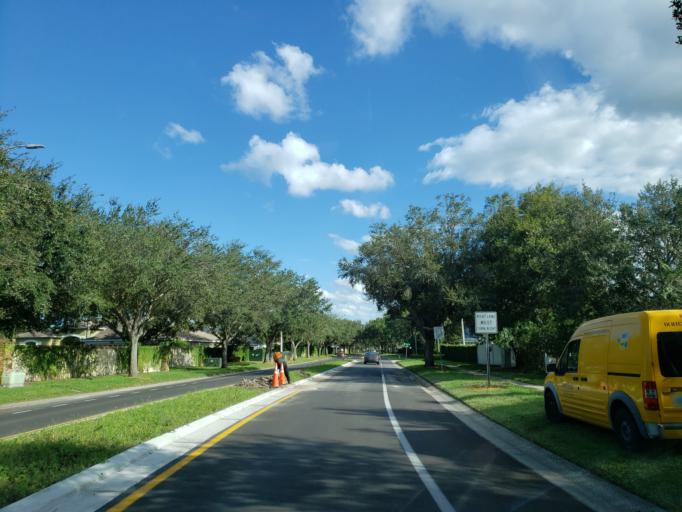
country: US
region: Florida
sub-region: Hillsborough County
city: Bloomingdale
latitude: 27.8757
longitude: -82.2597
